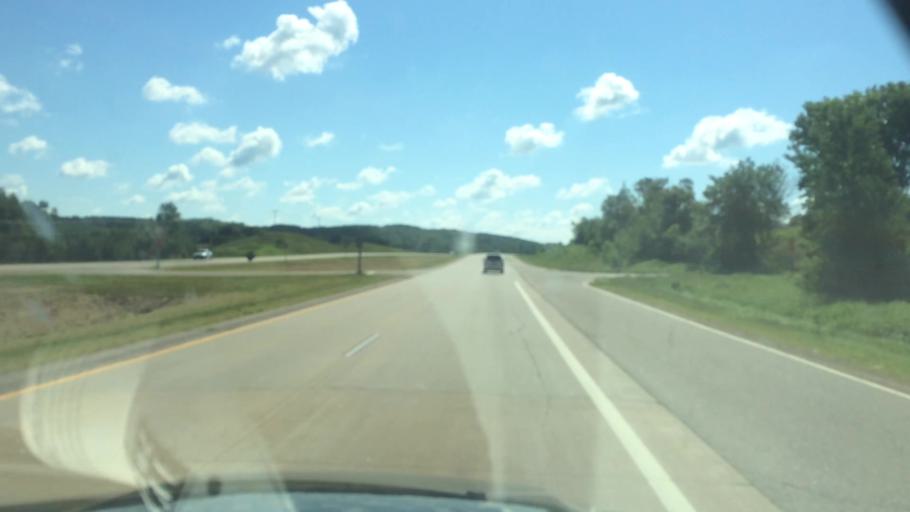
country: US
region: Wisconsin
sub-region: Portage County
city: Amherst
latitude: 44.5014
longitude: -89.3883
